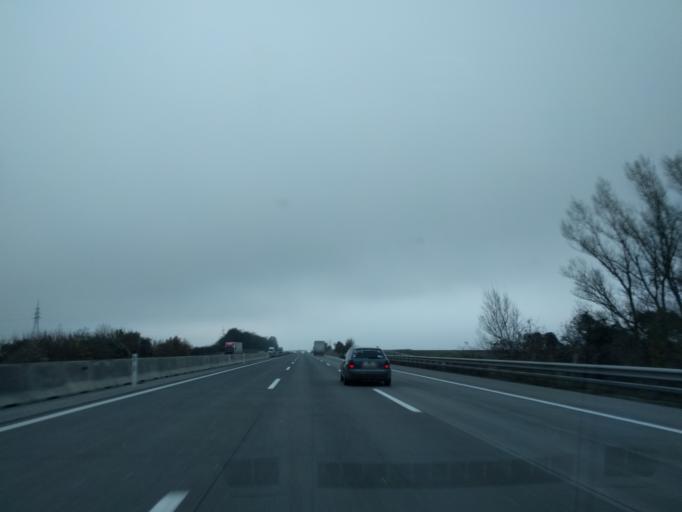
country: AT
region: Lower Austria
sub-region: Politischer Bezirk Sankt Polten
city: Haunoldstein
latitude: 48.1832
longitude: 15.4426
